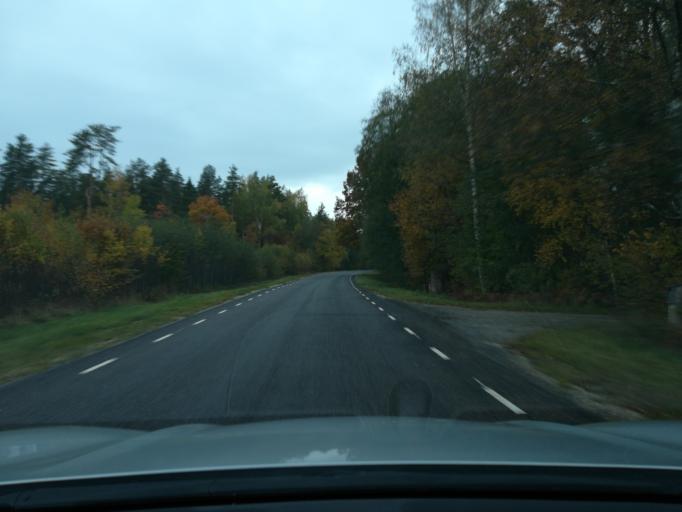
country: EE
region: Ida-Virumaa
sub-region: Johvi vald
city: Johvi
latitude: 59.0248
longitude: 27.3960
